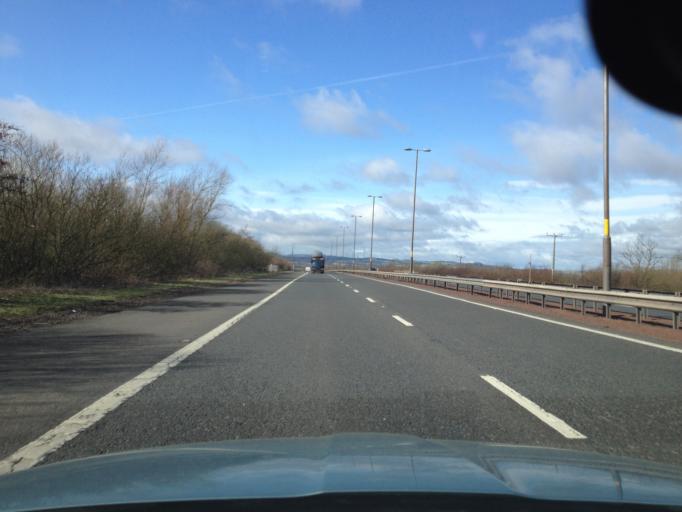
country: GB
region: Scotland
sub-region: Edinburgh
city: Newbridge
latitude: 55.9260
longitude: -3.3989
